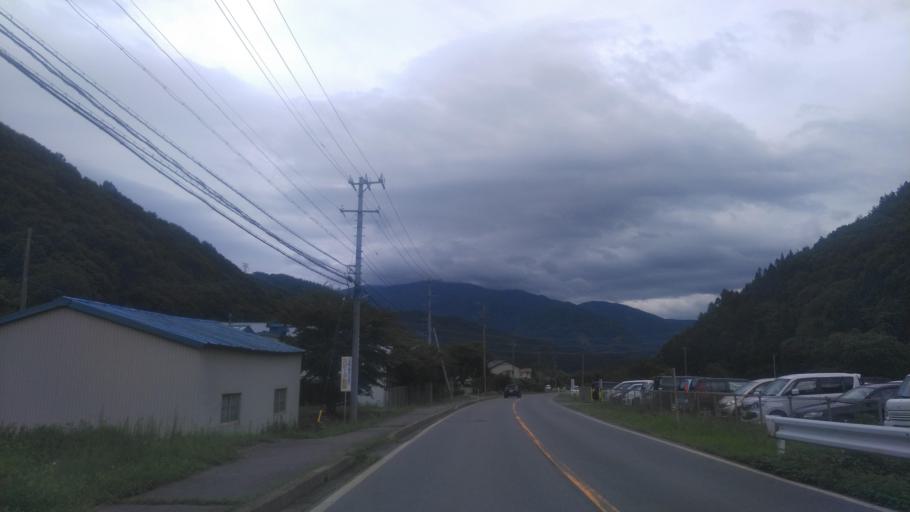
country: JP
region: Nagano
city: Ueda
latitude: 36.4614
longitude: 138.2750
